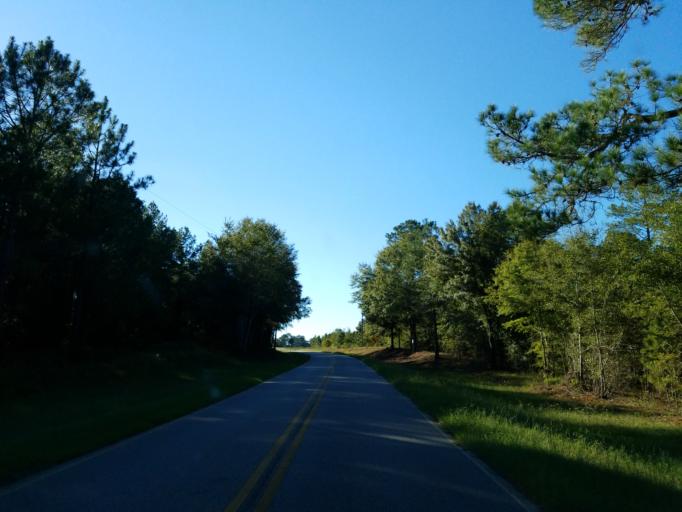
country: US
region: Georgia
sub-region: Lee County
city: Leesburg
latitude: 31.9127
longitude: -84.0305
